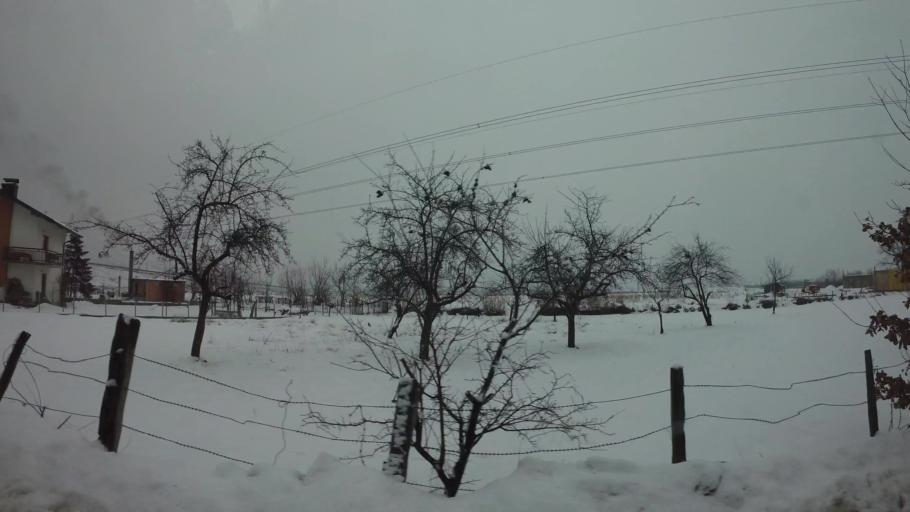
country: BA
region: Federation of Bosnia and Herzegovina
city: Hadzici
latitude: 43.8613
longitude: 18.2713
